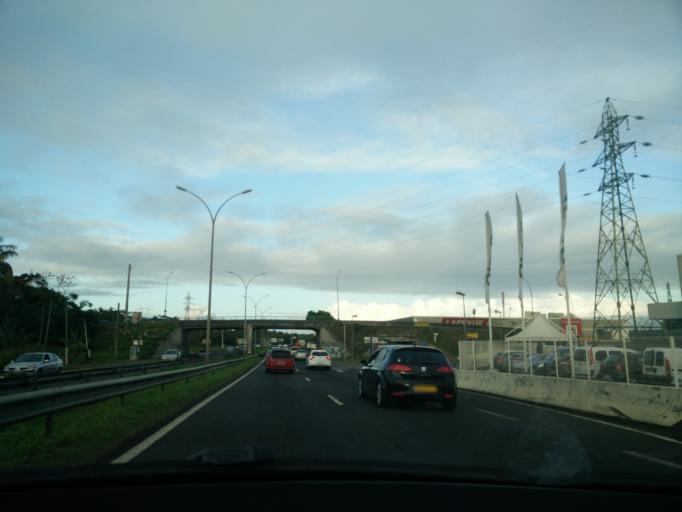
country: GP
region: Guadeloupe
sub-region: Guadeloupe
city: Pointe-a-Pitre
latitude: 16.2544
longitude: -61.5550
